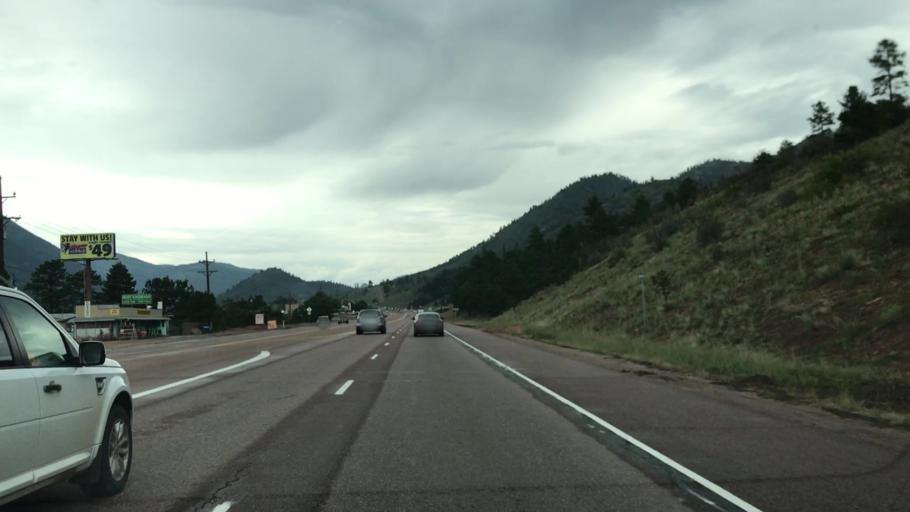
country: US
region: Colorado
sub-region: El Paso County
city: Cascade-Chipita Park
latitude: 38.9144
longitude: -104.9796
